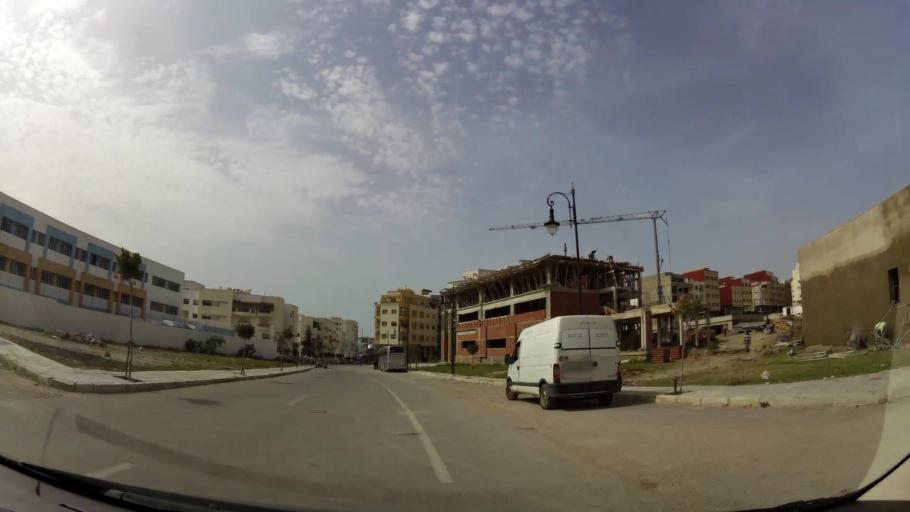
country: MA
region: Tanger-Tetouan
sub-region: Tanger-Assilah
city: Tangier
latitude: 35.7429
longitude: -5.8391
